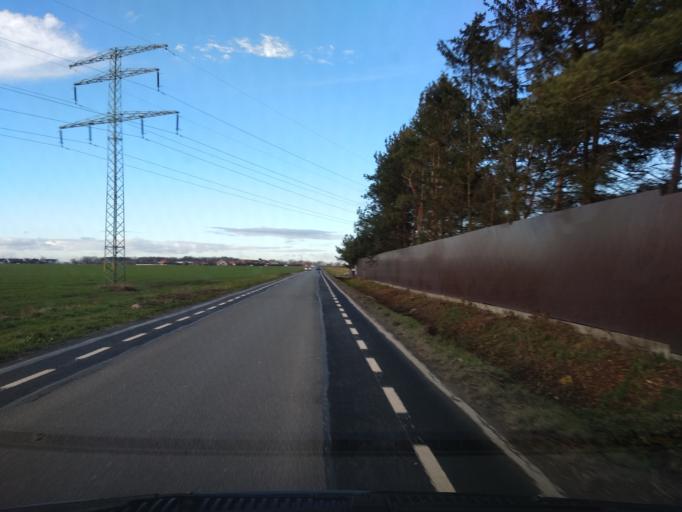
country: PL
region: Lower Silesian Voivodeship
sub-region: Powiat wroclawski
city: Zerniki Wroclawskie
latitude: 51.0436
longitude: 17.0569
